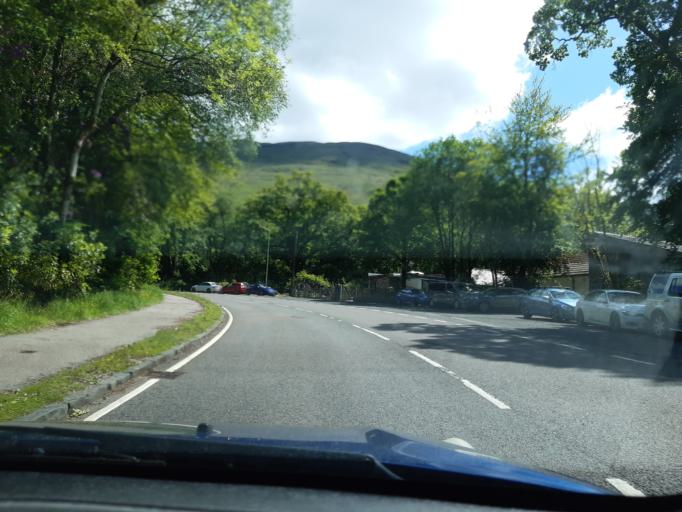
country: GB
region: Scotland
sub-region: Argyll and Bute
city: Garelochhead
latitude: 56.1982
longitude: -4.7448
